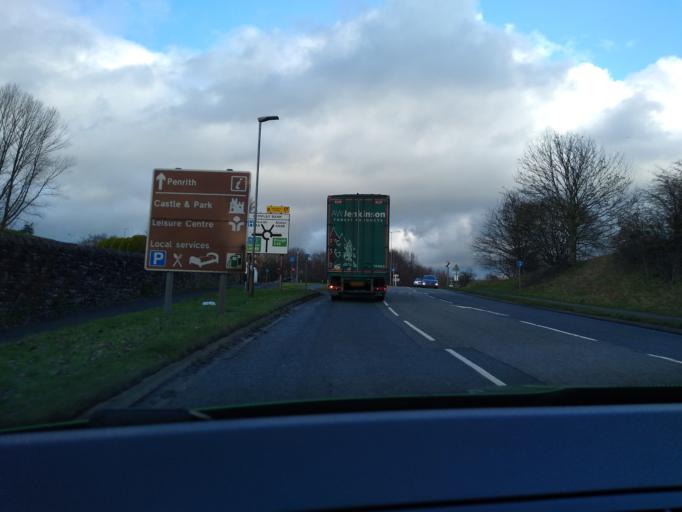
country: GB
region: England
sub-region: Cumbria
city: Penrith
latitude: 54.6530
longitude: -2.7425
